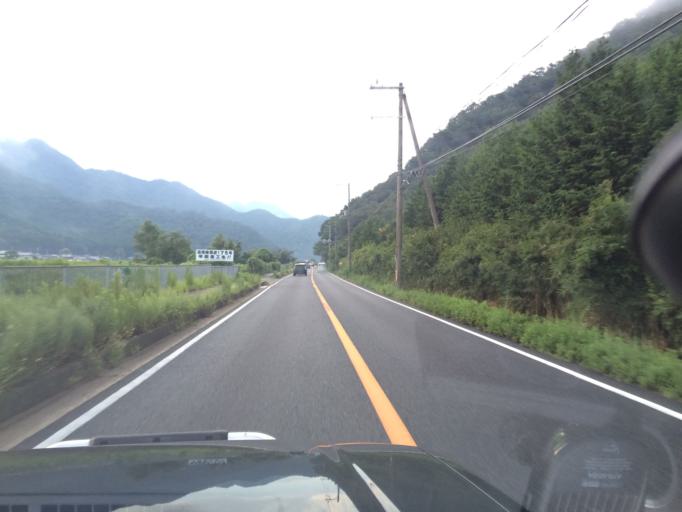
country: JP
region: Hyogo
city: Nishiwaki
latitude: 35.1259
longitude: 135.0085
